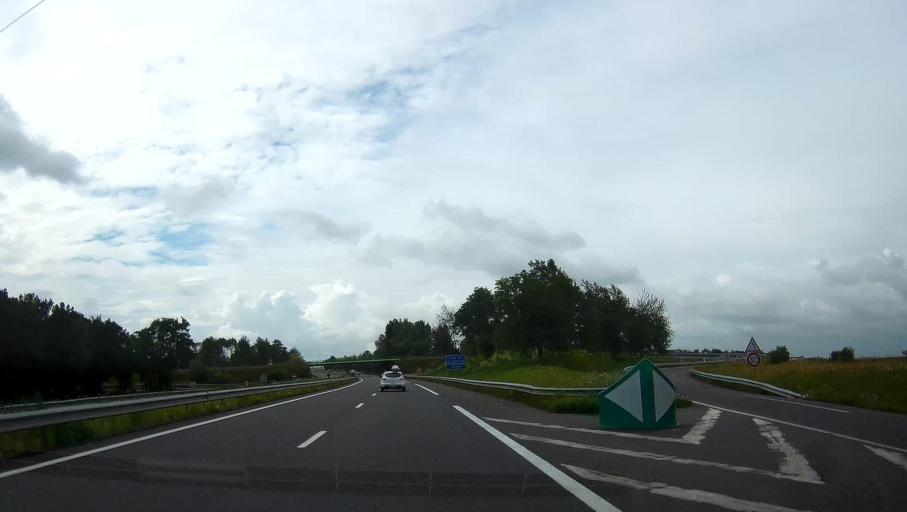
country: FR
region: Champagne-Ardenne
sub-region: Departement de la Marne
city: Fagnieres
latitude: 48.9726
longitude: 4.2841
